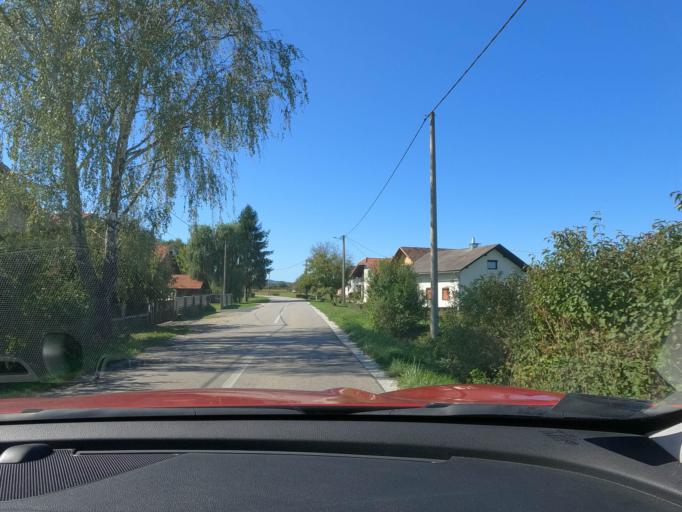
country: HR
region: Sisacko-Moslavacka
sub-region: Grad Sisak
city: Sisak
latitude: 45.4883
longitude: 16.3364
